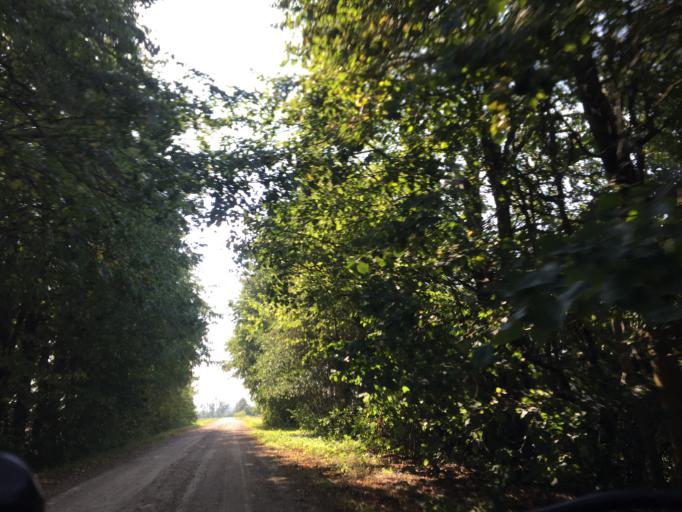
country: LV
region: Jelgava
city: Jelgava
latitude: 56.4560
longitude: 23.7008
